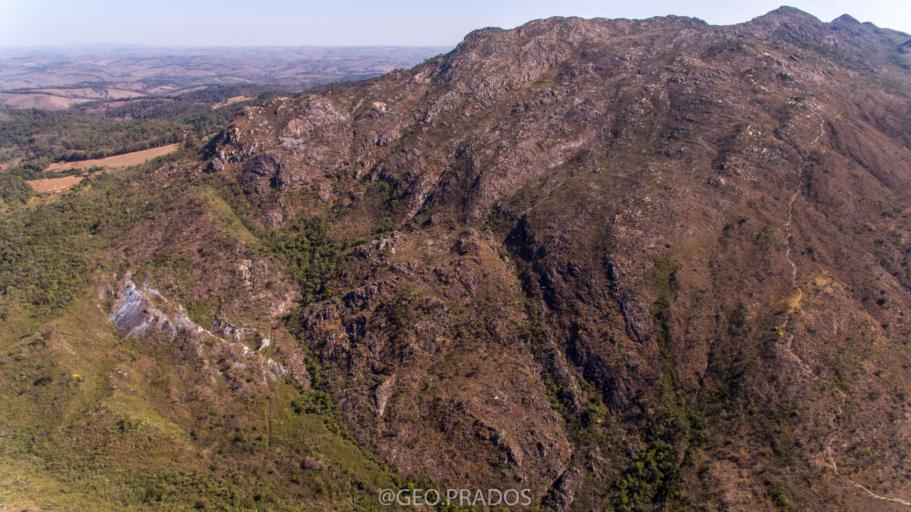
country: BR
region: Minas Gerais
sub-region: Tiradentes
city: Tiradentes
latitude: -21.0532
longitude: -44.1062
